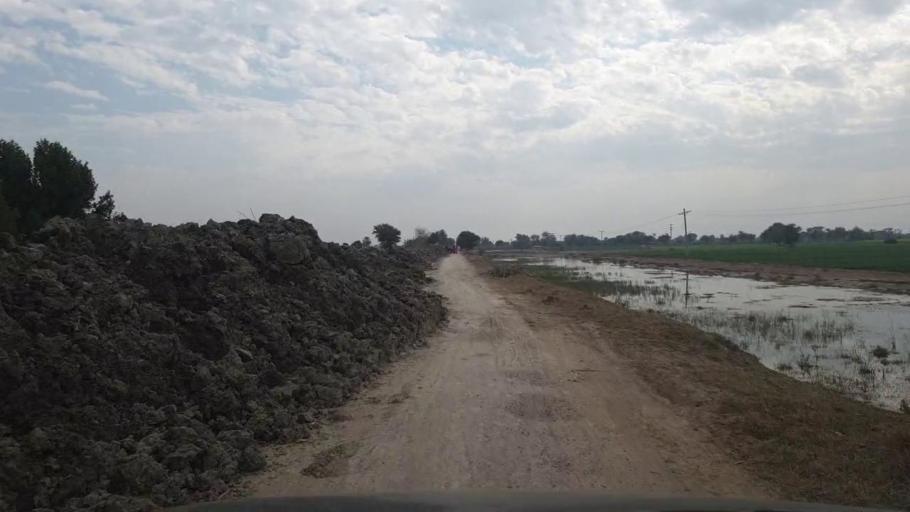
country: PK
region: Sindh
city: Sakrand
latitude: 26.0274
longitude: 68.4264
